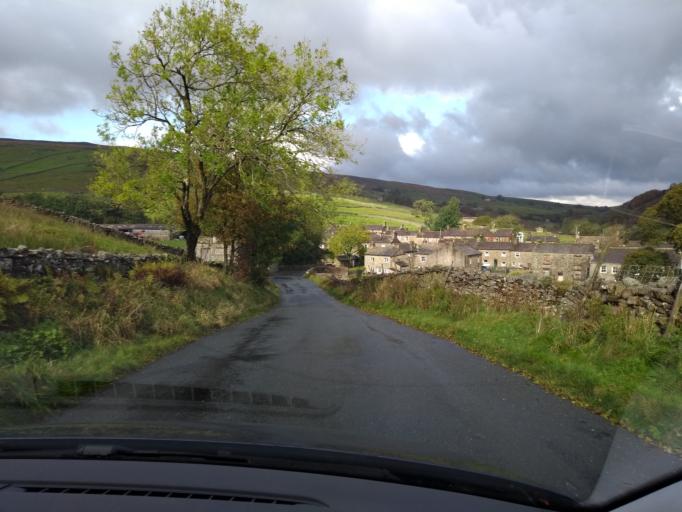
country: GB
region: England
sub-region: Cumbria
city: Kirkby Stephen
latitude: 54.3780
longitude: -2.1670
